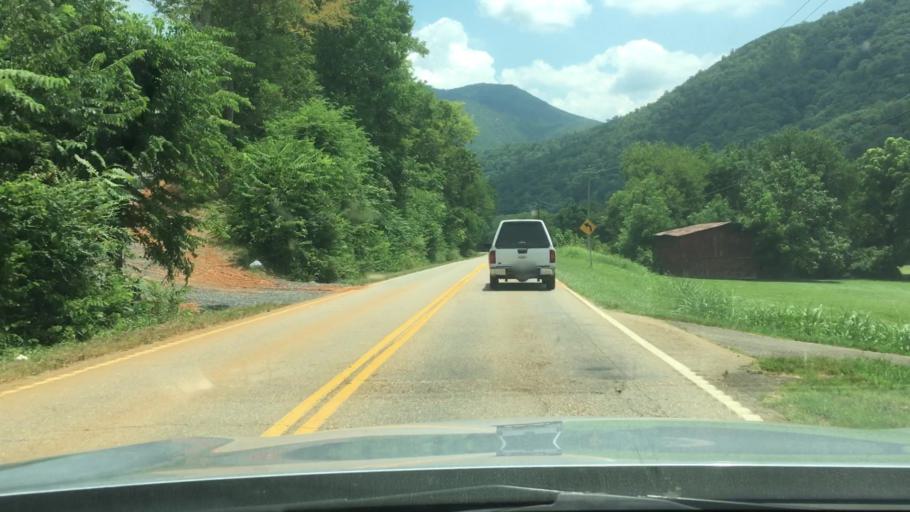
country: US
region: Tennessee
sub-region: Cocke County
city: Newport
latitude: 35.9461
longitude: -83.0971
